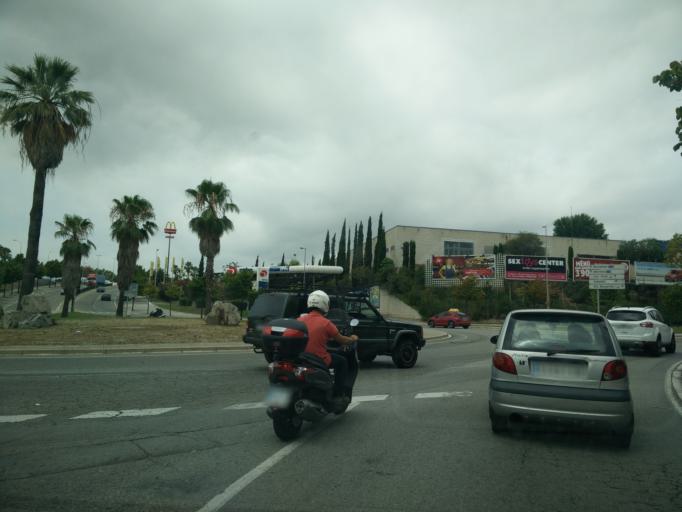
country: ES
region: Catalonia
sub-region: Provincia de Barcelona
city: Terrassa
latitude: 41.5459
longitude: 2.0288
